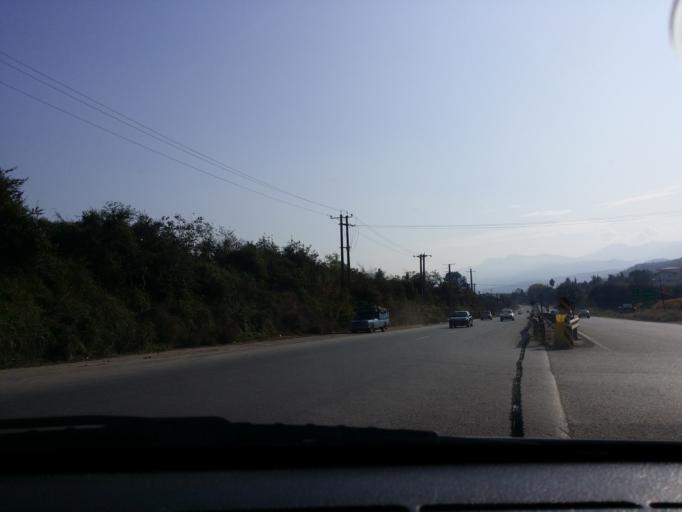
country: IR
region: Mazandaran
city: Chalus
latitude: 36.6409
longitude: 51.4329
